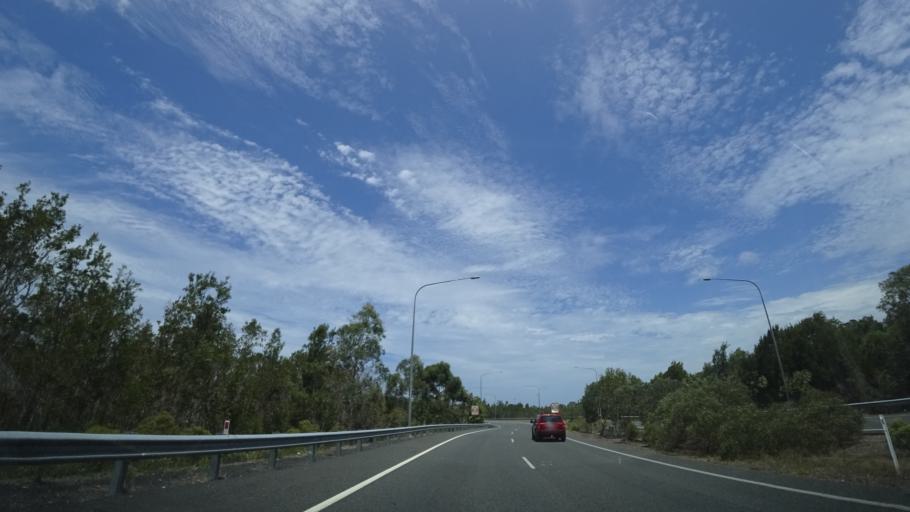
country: AU
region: Queensland
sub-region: Sunshine Coast
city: Buderim
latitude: -26.6105
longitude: 153.0820
